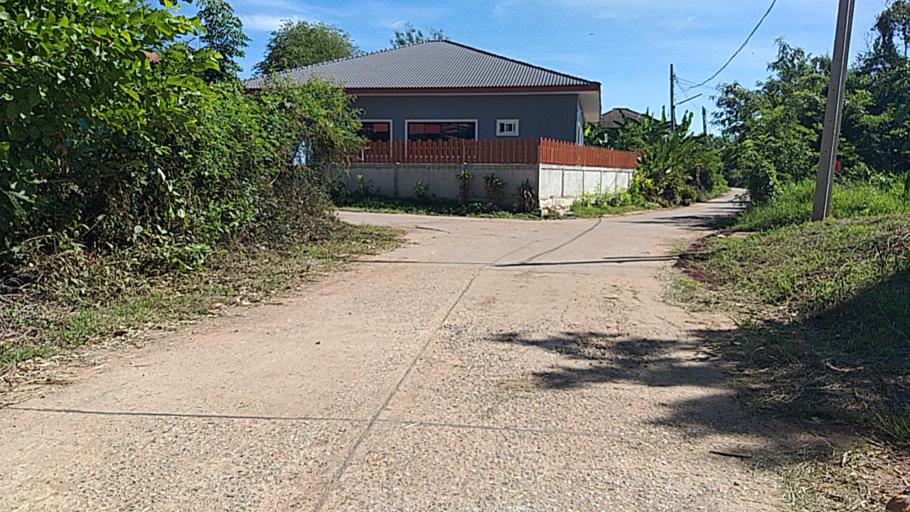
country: TH
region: Chaiyaphum
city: Ban Thaen
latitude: 16.4059
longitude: 102.3540
